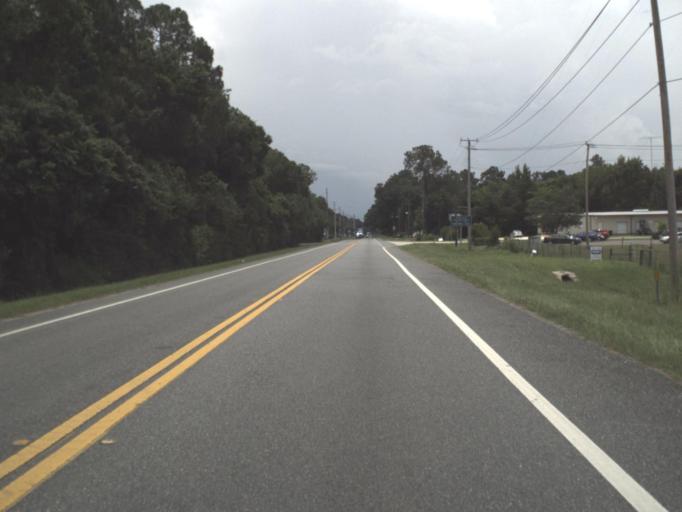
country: US
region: Florida
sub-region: Bradford County
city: Starke
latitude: 29.9336
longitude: -82.1043
